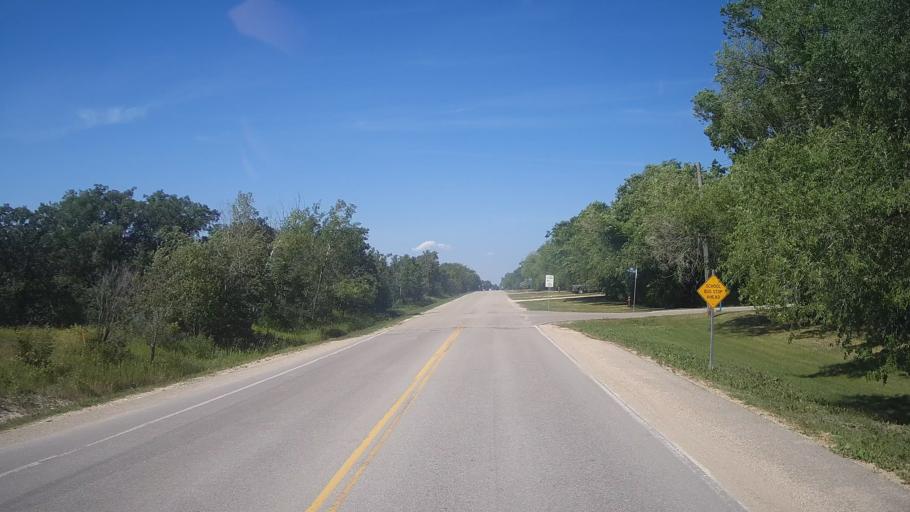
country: CA
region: Manitoba
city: Stonewall
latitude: 50.1235
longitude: -97.3333
